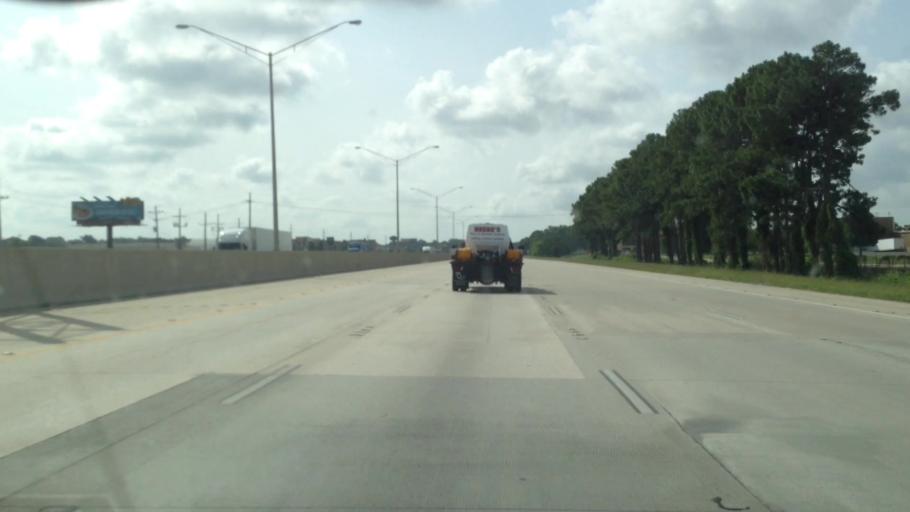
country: US
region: Louisiana
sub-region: East Baton Rouge Parish
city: Village Saint George
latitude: 30.3793
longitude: -91.0615
